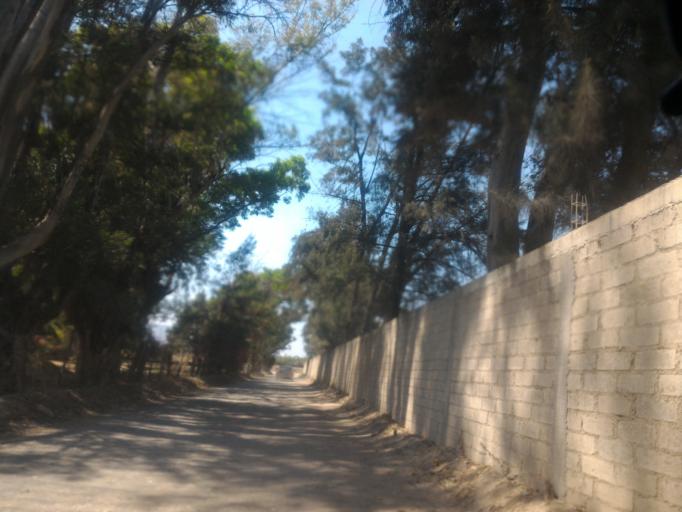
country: MX
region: Jalisco
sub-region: San Pedro Tlaquepaque
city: Paseo del Prado
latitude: 20.5617
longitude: -103.4001
